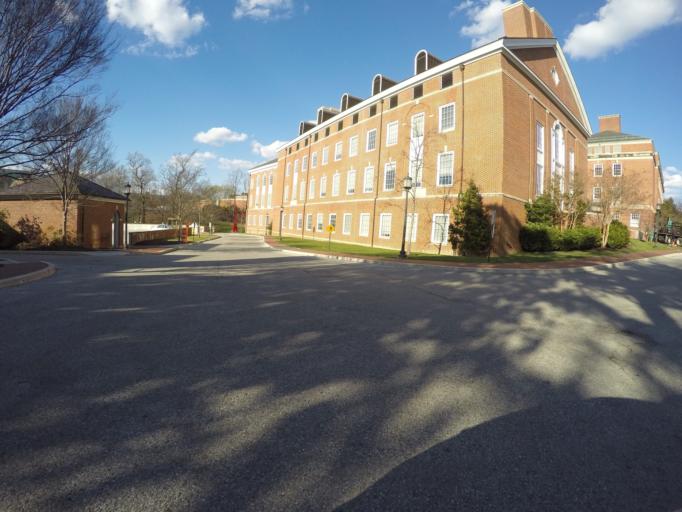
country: US
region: Maryland
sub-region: City of Baltimore
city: Baltimore
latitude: 39.3299
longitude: -76.6228
